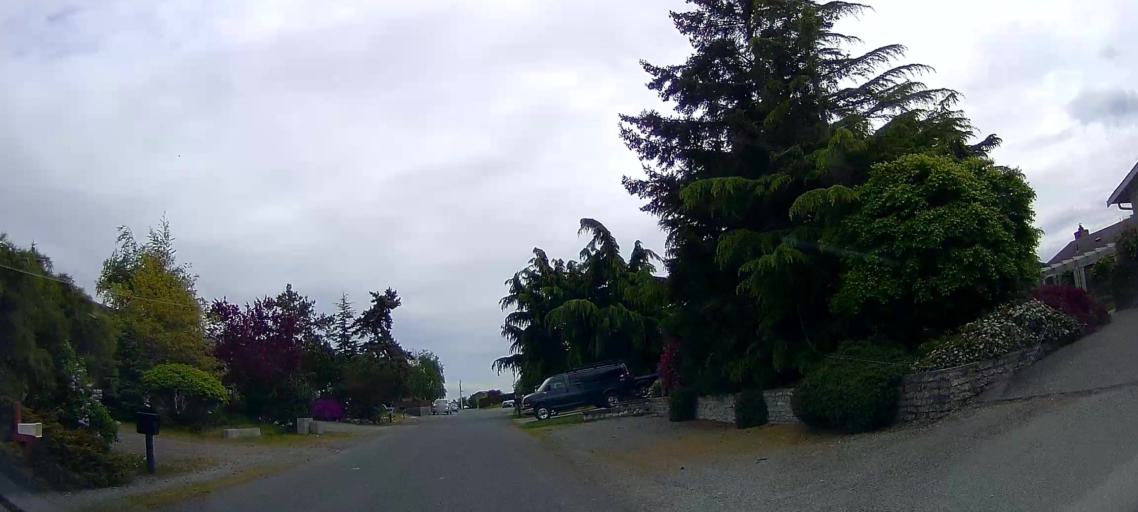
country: US
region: Washington
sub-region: Skagit County
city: Anacortes
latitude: 48.4316
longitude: -122.4971
